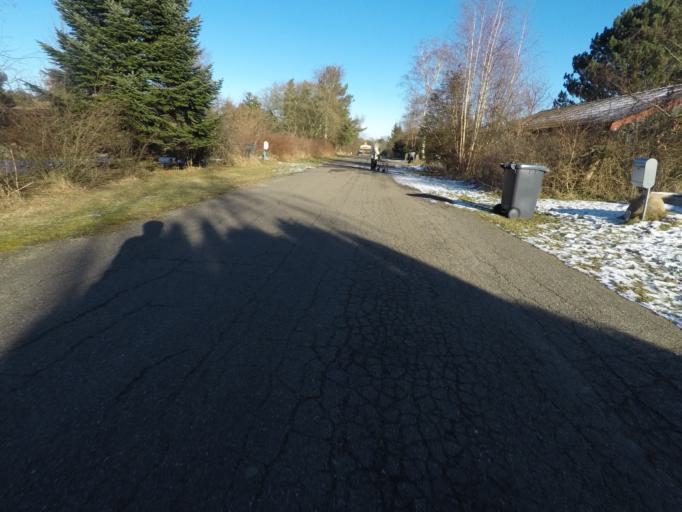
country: DK
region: Capital Region
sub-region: Halsnaes Kommune
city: Liseleje
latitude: 56.0008
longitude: 11.9367
